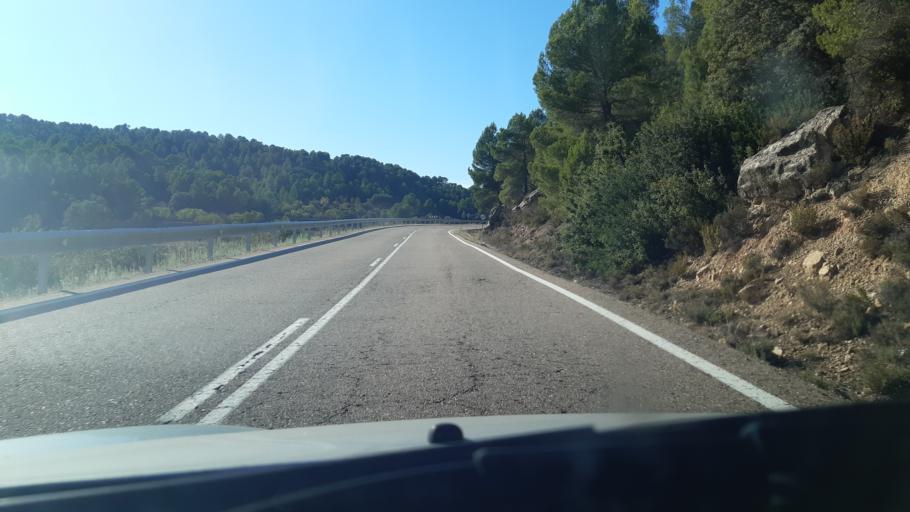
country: ES
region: Aragon
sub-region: Provincia de Teruel
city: Valjunquera
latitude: 40.9459
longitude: 0.0524
